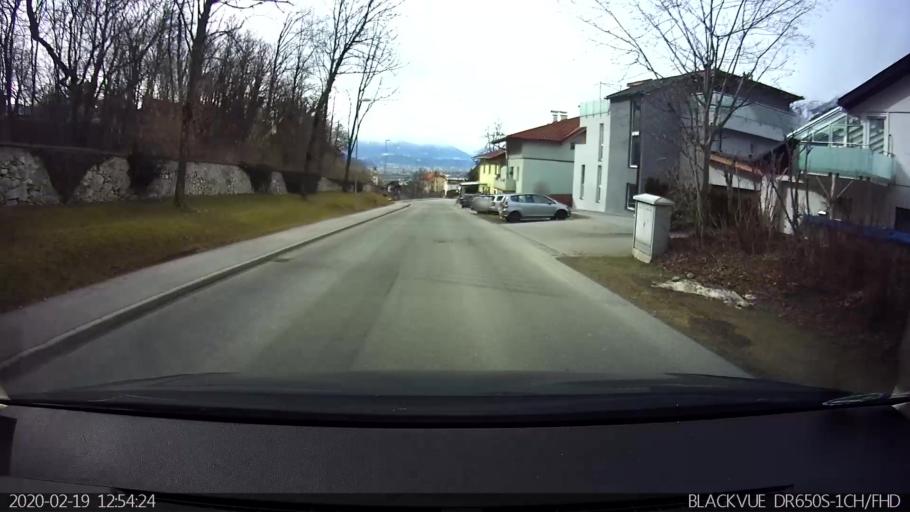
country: AT
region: Tyrol
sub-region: Politischer Bezirk Innsbruck Land
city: Absam
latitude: 47.2999
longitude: 11.5105
